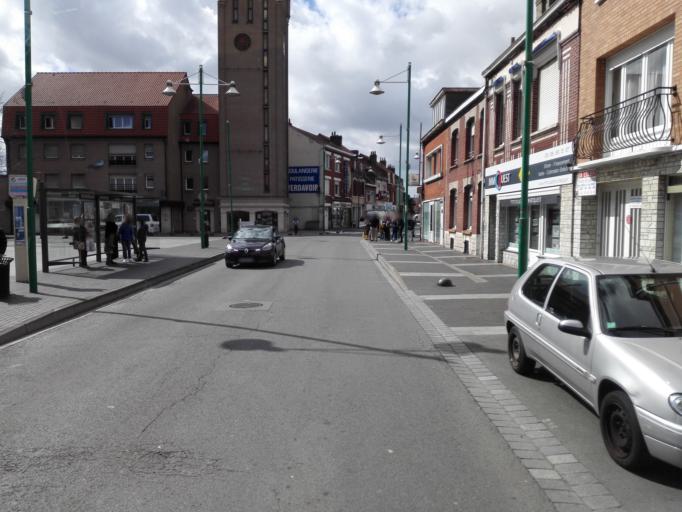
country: FR
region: Nord-Pas-de-Calais
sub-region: Departement du Nord
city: Saint-Pol-sur-Mer
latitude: 51.0287
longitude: 2.3527
